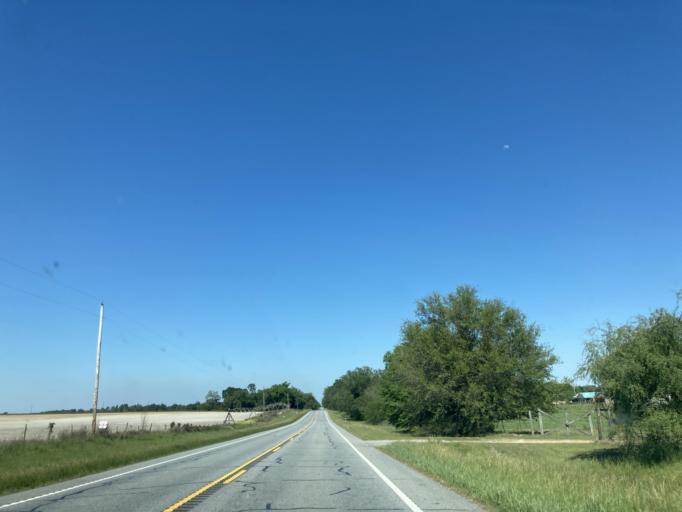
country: US
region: Georgia
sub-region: Baker County
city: Newton
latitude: 31.2606
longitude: -84.4085
